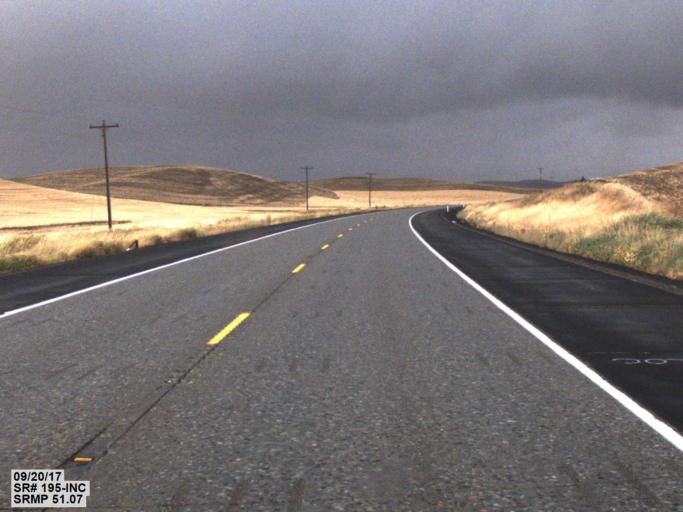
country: US
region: Washington
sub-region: Whitman County
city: Colfax
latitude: 47.0463
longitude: -117.3784
